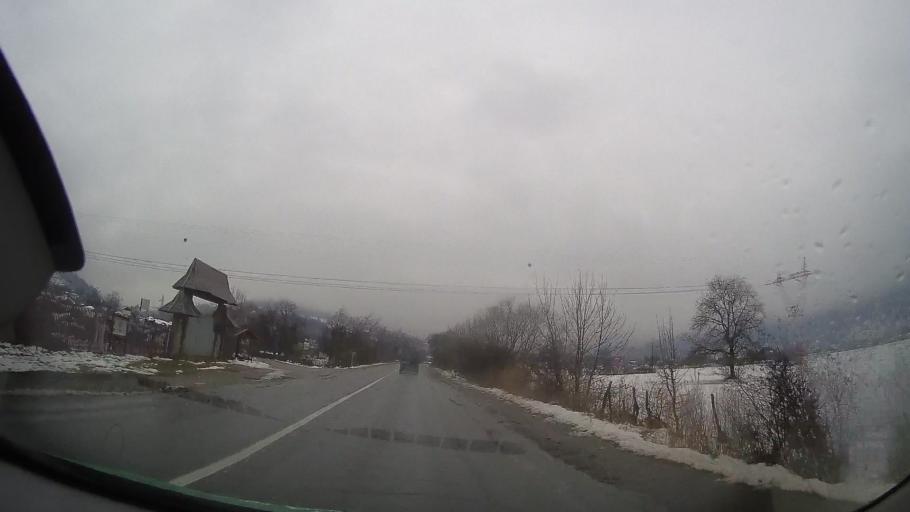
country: RO
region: Neamt
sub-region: Comuna Pangarati
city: Stejaru
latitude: 46.9194
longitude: 26.1890
